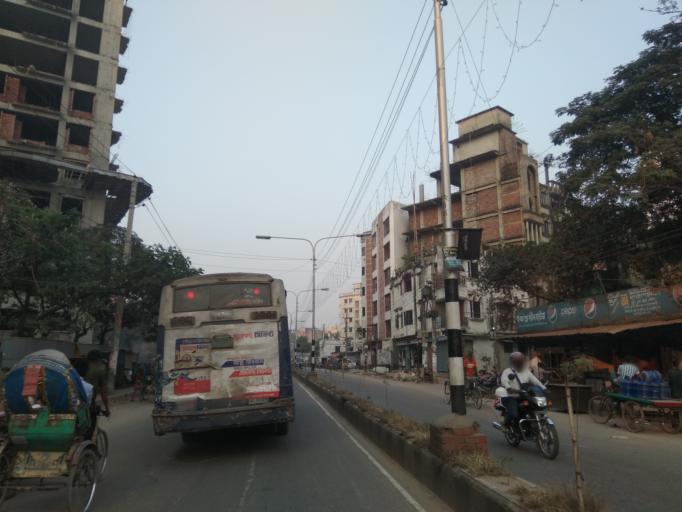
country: BD
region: Dhaka
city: Azimpur
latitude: 23.8129
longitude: 90.3613
